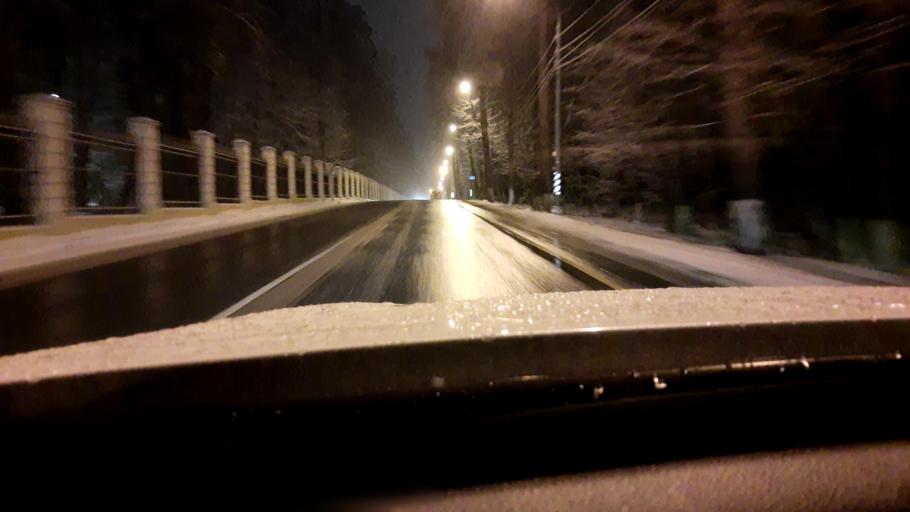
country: RU
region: Moskovskaya
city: Arkhangel'skoye
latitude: 55.7922
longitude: 37.2837
